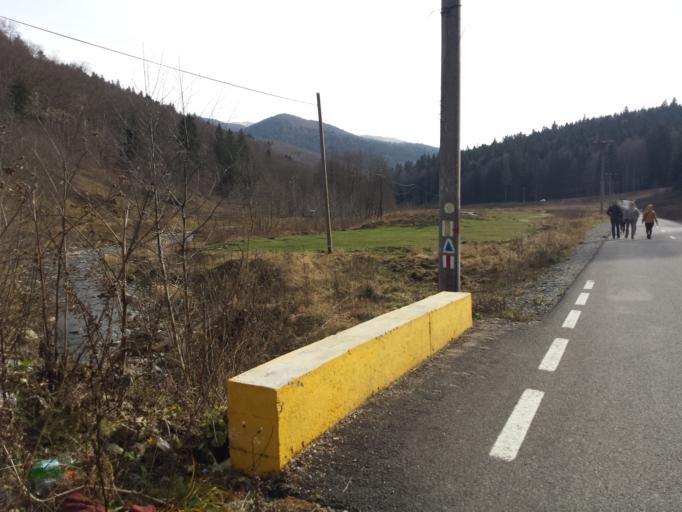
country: RO
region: Prahova
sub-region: Oras Azuga
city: Azuga
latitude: 45.4335
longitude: 25.5303
